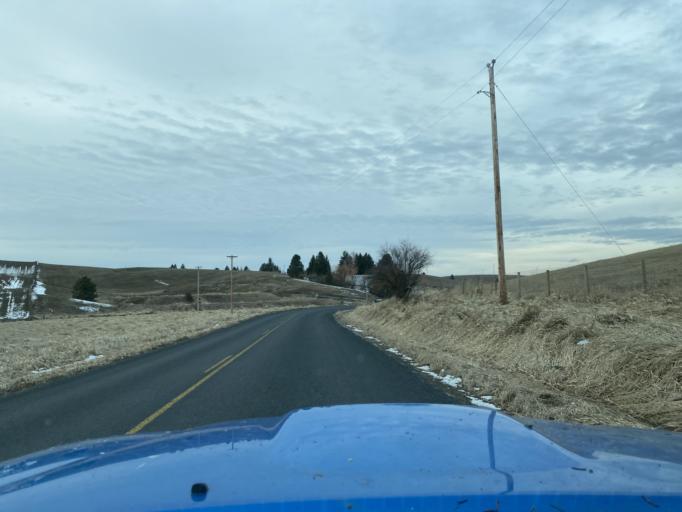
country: US
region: Idaho
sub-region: Latah County
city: Moscow
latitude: 46.7048
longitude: -116.9464
